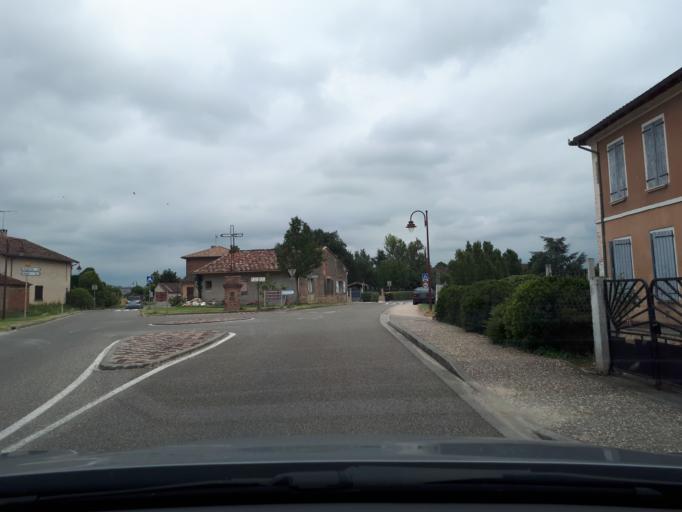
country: FR
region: Midi-Pyrenees
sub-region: Departement du Tarn-et-Garonne
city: Campsas
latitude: 43.8964
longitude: 1.3267
